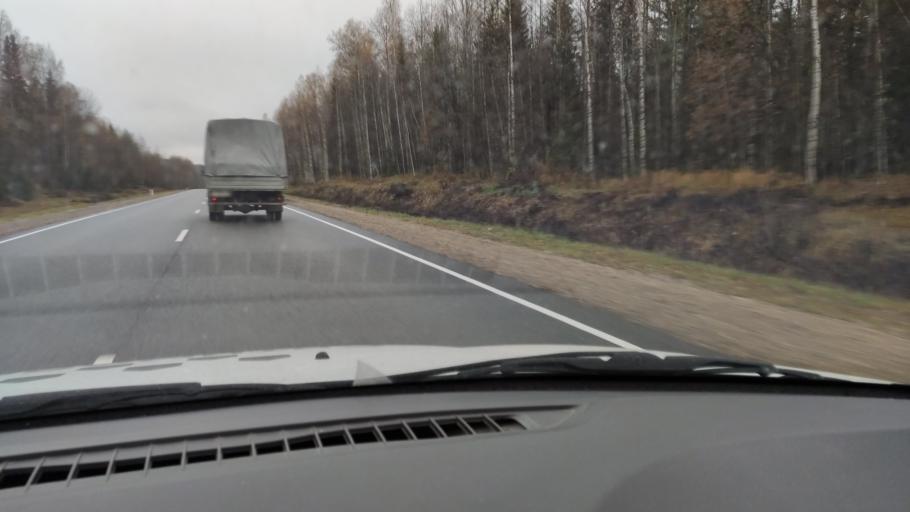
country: RU
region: Kirov
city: Chernaya Kholunitsa
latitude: 58.7863
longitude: 51.8998
